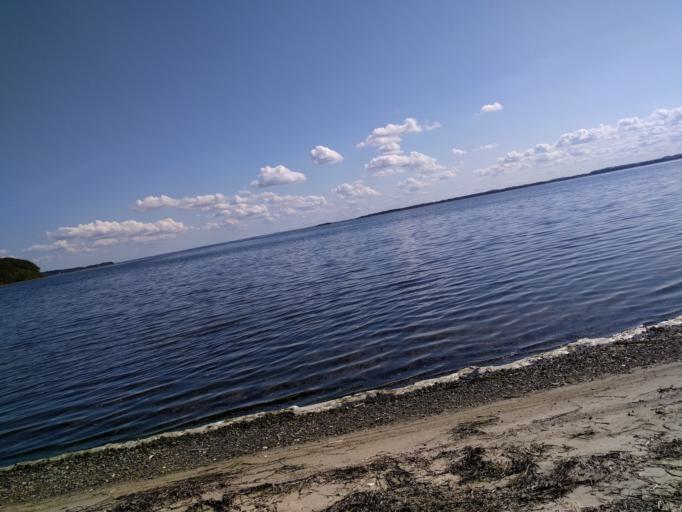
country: DK
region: Central Jutland
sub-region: Skive Kommune
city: Hojslev
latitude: 56.6650
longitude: 9.0951
